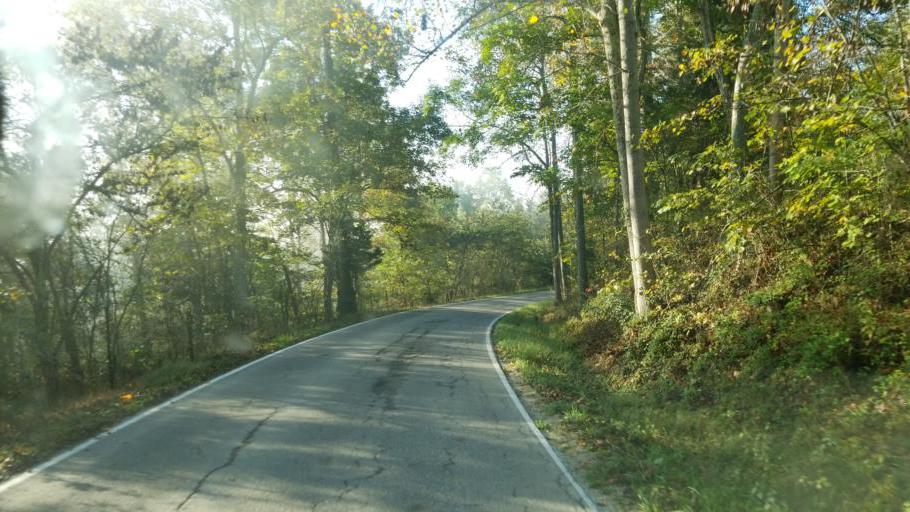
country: US
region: Ohio
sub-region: Adams County
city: Manchester
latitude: 38.5136
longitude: -83.5221
